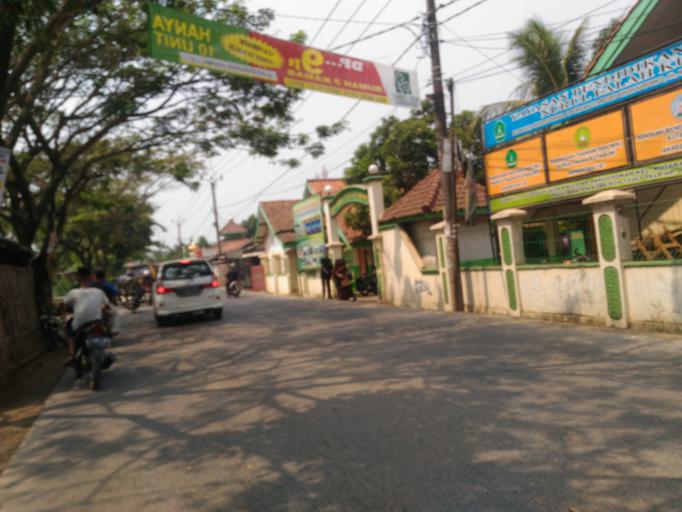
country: ID
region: West Java
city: Sepatan
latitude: -6.1472
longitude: 106.5715
